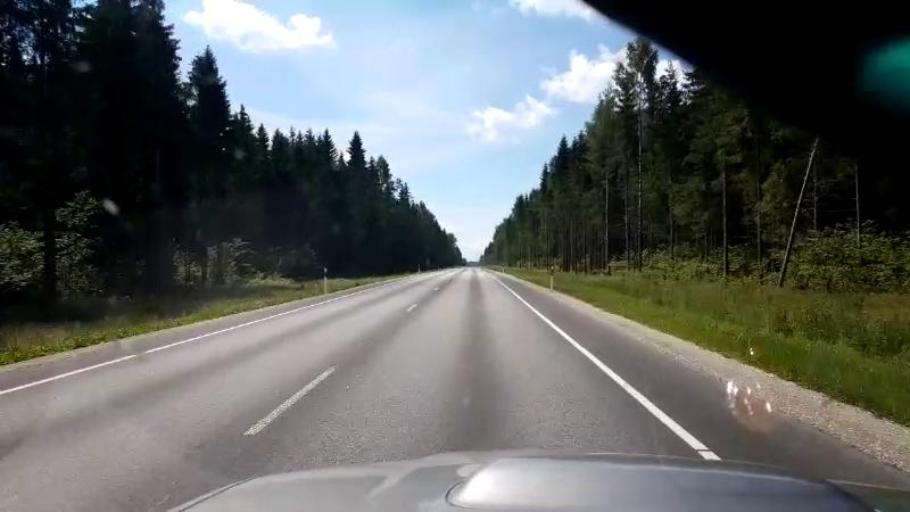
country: EE
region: Jaervamaa
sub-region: Paide linn
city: Paide
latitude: 58.9586
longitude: 25.6549
